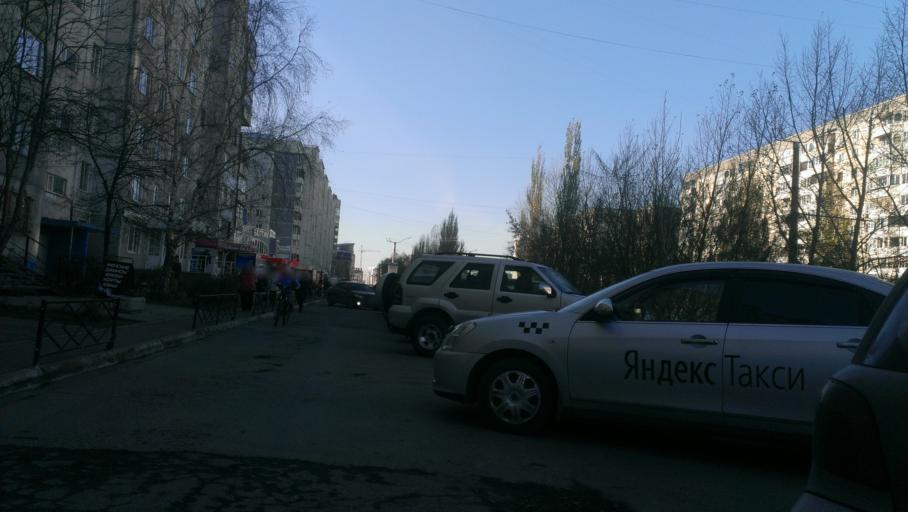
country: RU
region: Altai Krai
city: Novosilikatnyy
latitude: 53.3353
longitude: 83.6746
